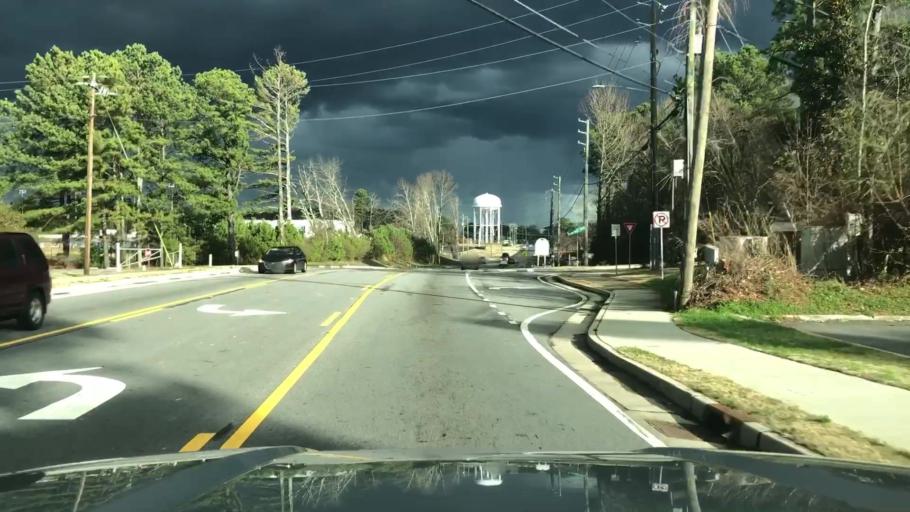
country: US
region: Georgia
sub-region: Fulton County
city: College Park
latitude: 33.6082
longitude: -84.4438
